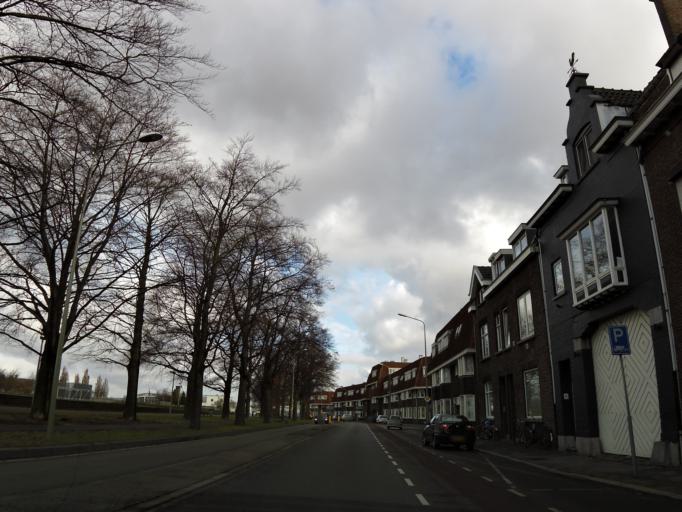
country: NL
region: Limburg
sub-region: Gemeente Maastricht
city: Maastricht
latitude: 50.8546
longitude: 5.6991
